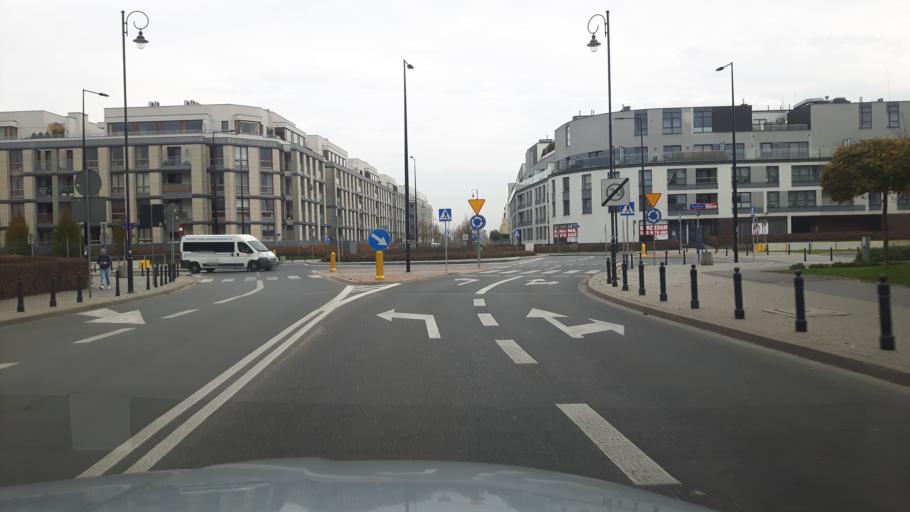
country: PL
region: Masovian Voivodeship
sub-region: Warszawa
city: Wilanow
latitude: 52.1584
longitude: 21.0805
